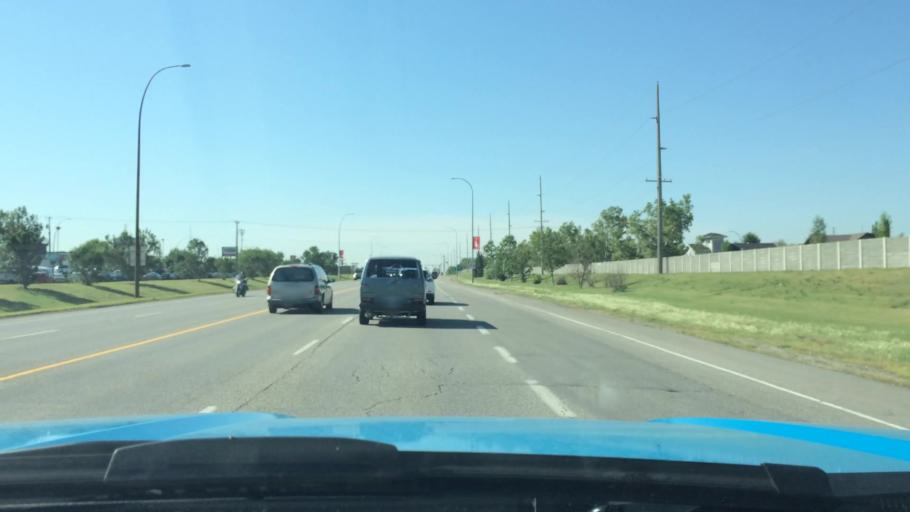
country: CA
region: Alberta
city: Calgary
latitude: 51.0632
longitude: -114.0018
